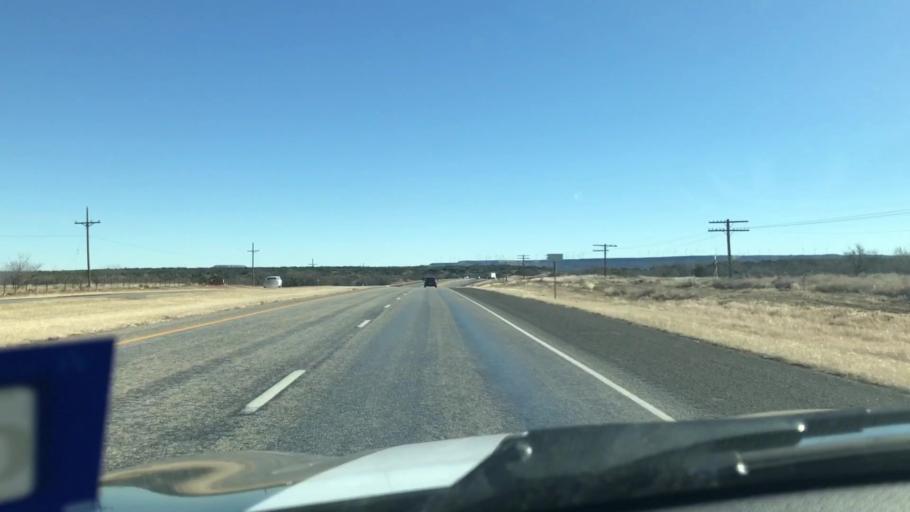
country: US
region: Texas
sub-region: Garza County
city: Post
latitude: 33.0300
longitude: -101.1887
